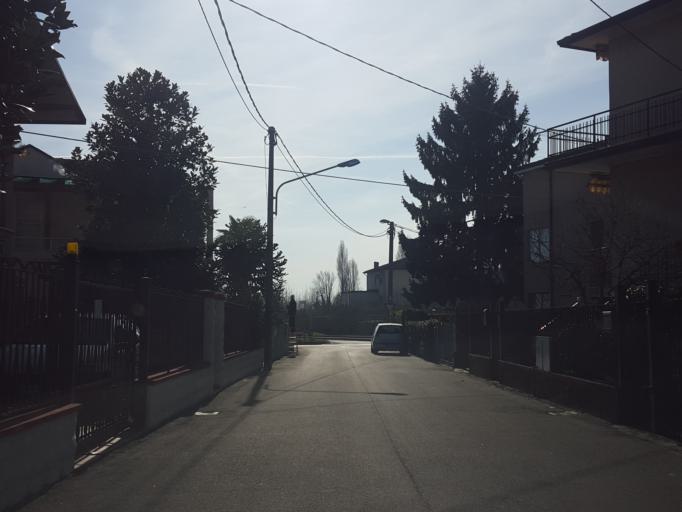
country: IT
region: Veneto
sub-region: Provincia di Vicenza
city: Villaggio Montegrappa
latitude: 45.5410
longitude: 11.5956
